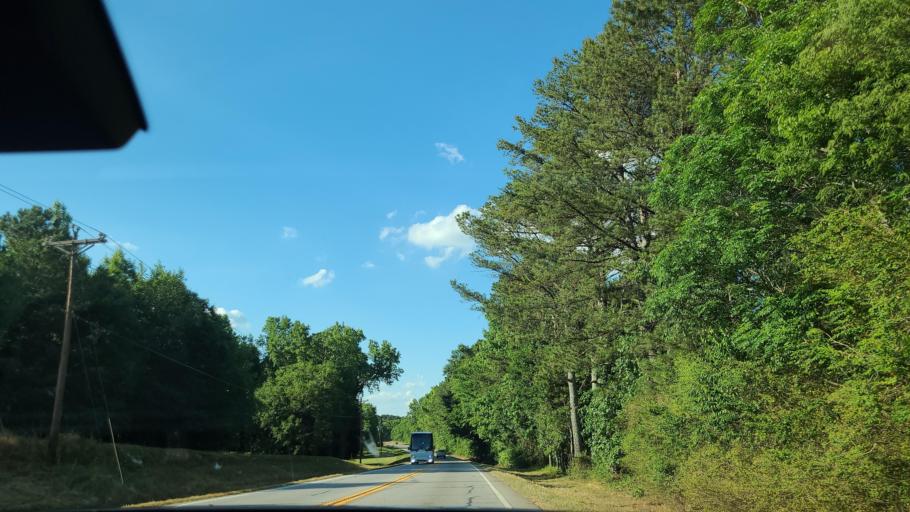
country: US
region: Georgia
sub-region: Oconee County
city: Watkinsville
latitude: 33.7802
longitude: -83.4240
